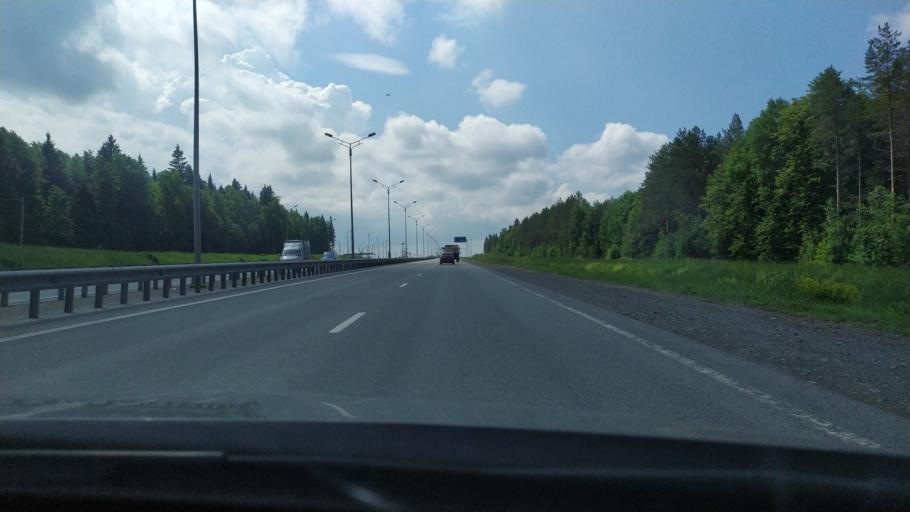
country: RU
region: Perm
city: Ferma
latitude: 58.0059
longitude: 56.3944
